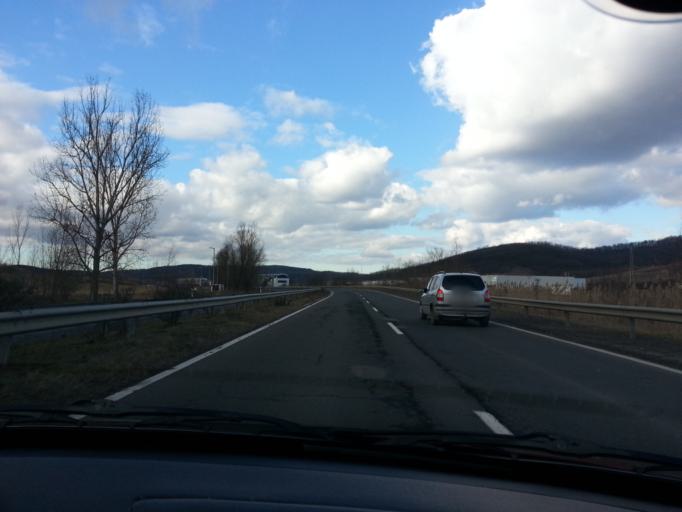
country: HU
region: Nograd
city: Salgotarjan
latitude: 48.0404
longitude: 19.7975
